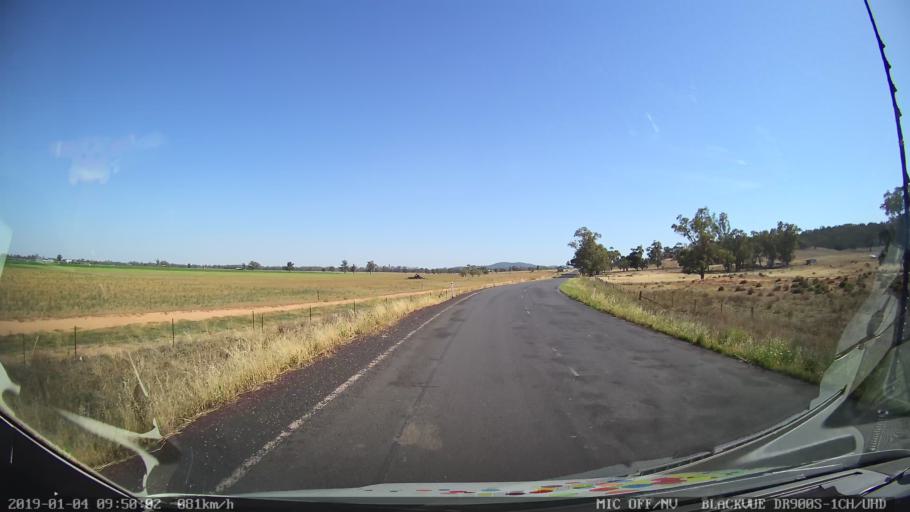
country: AU
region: New South Wales
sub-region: Cabonne
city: Canowindra
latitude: -33.5888
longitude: 148.4148
